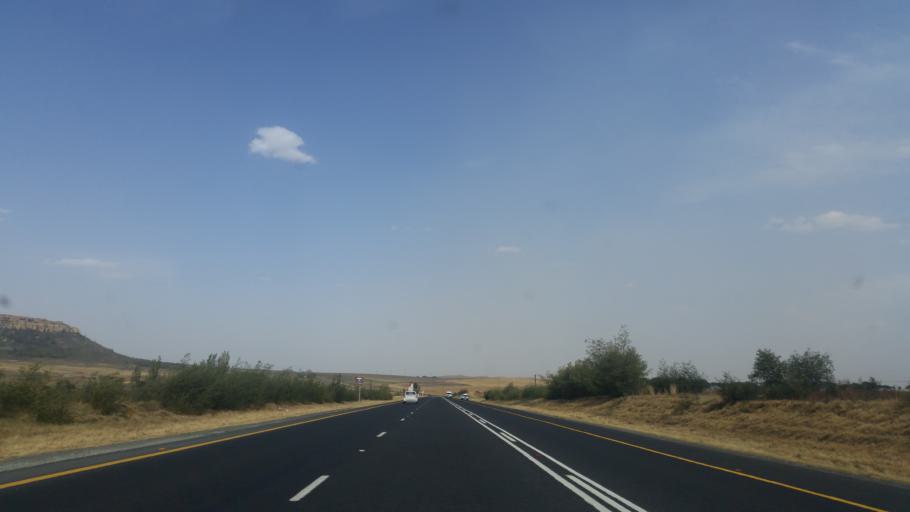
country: ZA
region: Orange Free State
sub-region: Thabo Mofutsanyana District Municipality
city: Bethlehem
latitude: -28.2979
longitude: 28.5412
